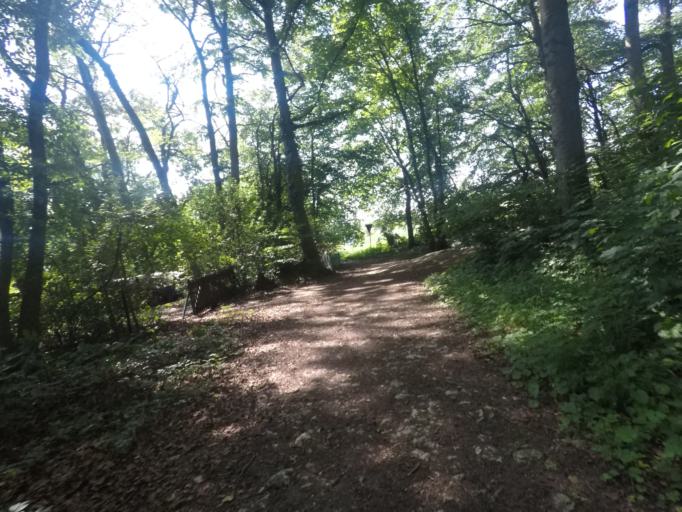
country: DE
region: North Rhine-Westphalia
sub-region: Regierungsbezirk Detmold
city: Bielefeld
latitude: 52.0035
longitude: 8.4952
